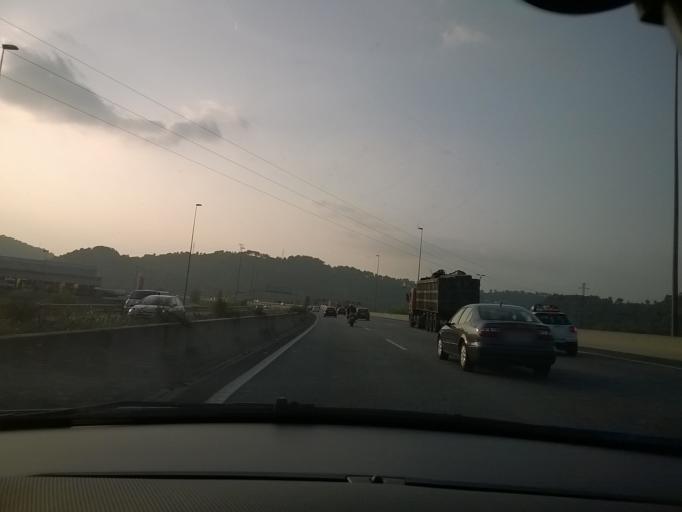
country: ES
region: Catalonia
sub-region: Provincia de Barcelona
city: Castellbisbal
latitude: 41.4703
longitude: 1.9632
